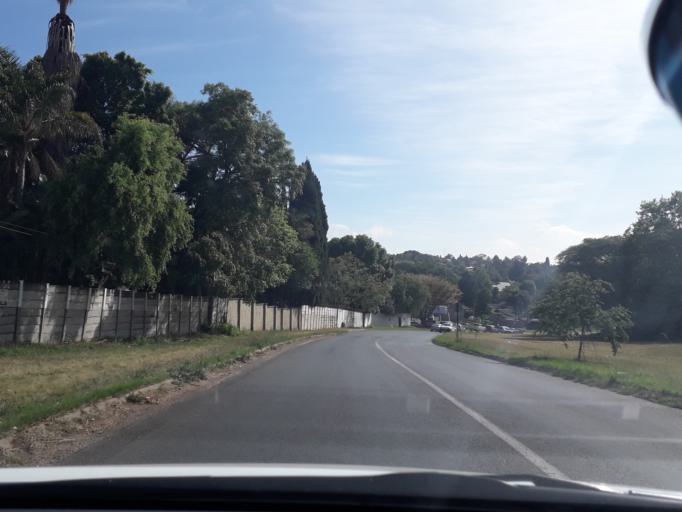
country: ZA
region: Gauteng
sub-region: City of Johannesburg Metropolitan Municipality
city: Roodepoort
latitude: -26.1207
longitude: 27.9239
